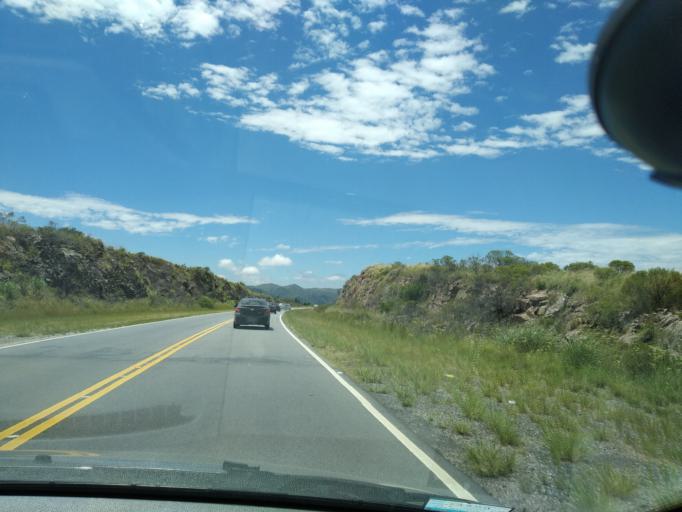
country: AR
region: Cordoba
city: Cuesta Blanca
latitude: -31.5843
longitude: -64.6239
